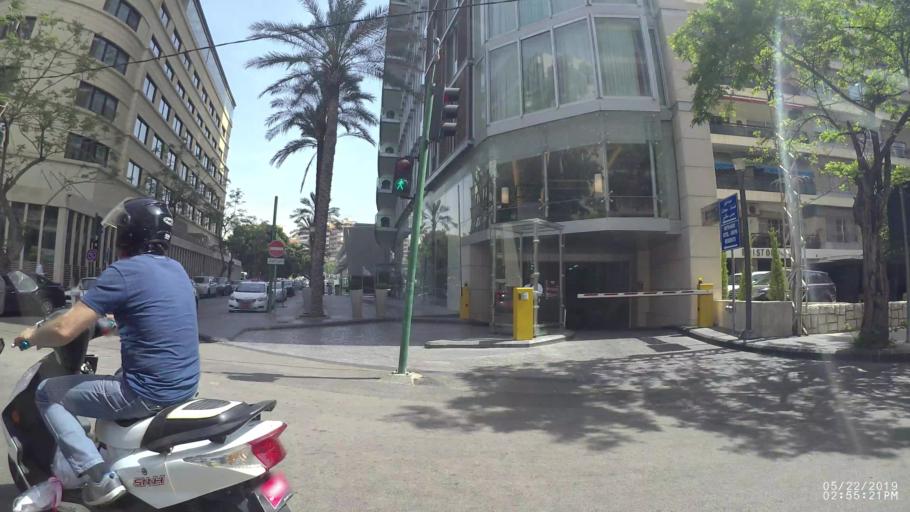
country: LB
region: Beyrouth
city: Ra's Bayrut
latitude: 33.8915
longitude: 35.4832
